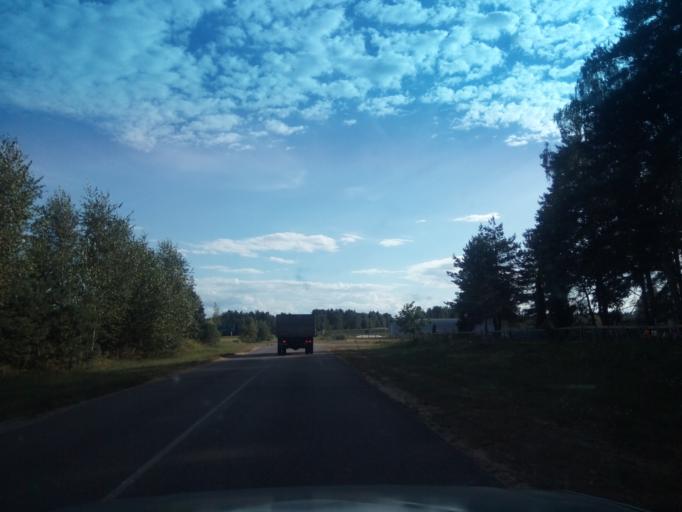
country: BY
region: Vitebsk
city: Polatsk
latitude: 55.4349
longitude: 28.7729
